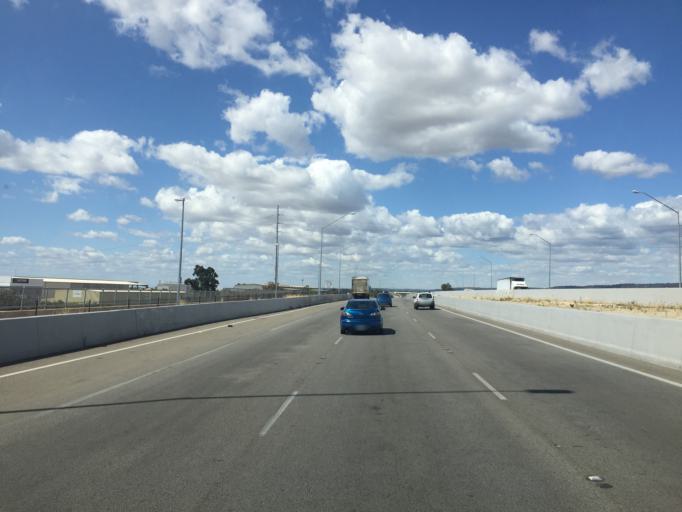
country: AU
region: Western Australia
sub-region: Canning
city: East Cannington
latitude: -31.9990
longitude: 115.9765
